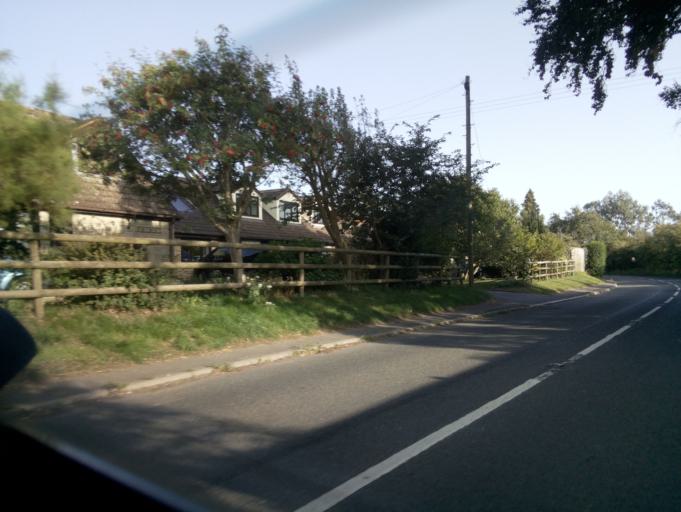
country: GB
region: England
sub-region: Gloucestershire
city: Tewkesbury
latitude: 51.9563
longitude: -2.2424
